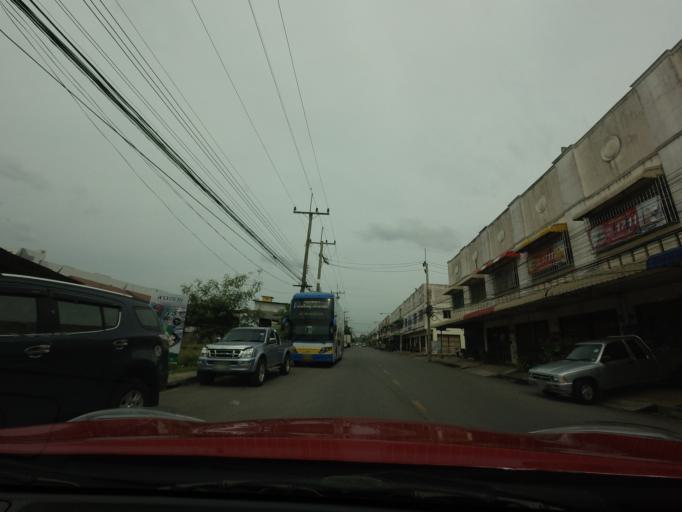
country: TH
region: Songkhla
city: Hat Yai
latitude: 6.9908
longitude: 100.4791
